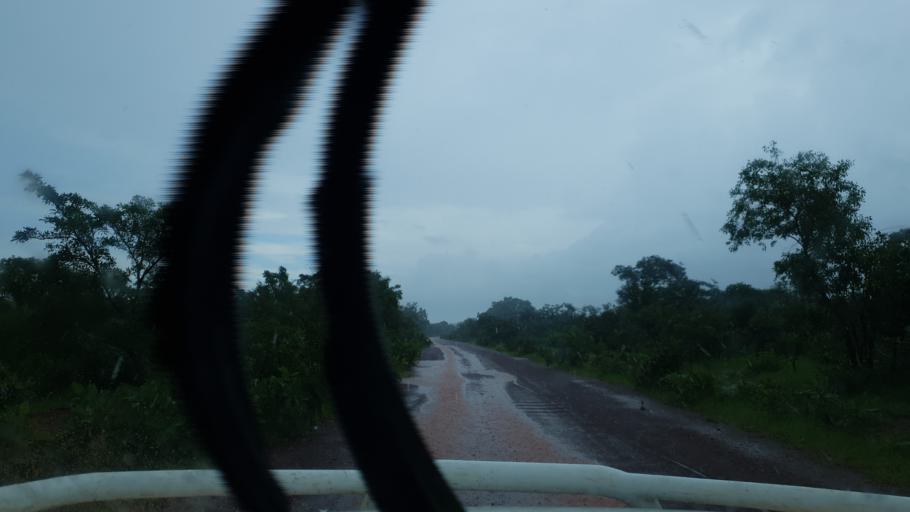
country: ML
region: Sikasso
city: Kolondieba
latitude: 11.6036
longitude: -6.6733
